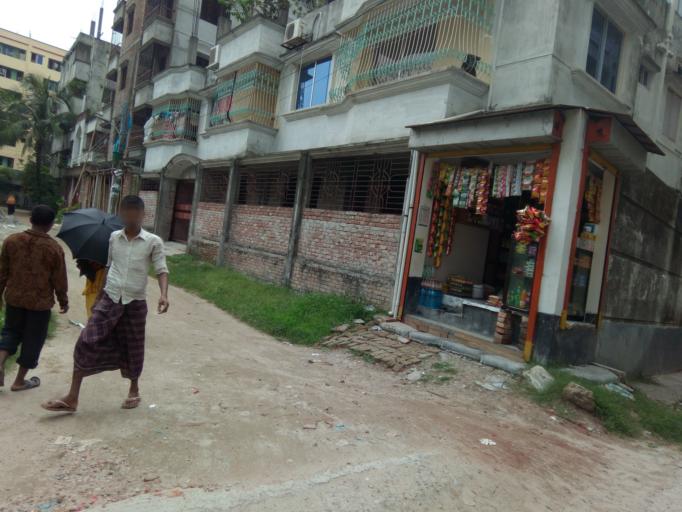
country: BD
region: Dhaka
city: Paltan
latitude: 23.7540
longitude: 90.4421
